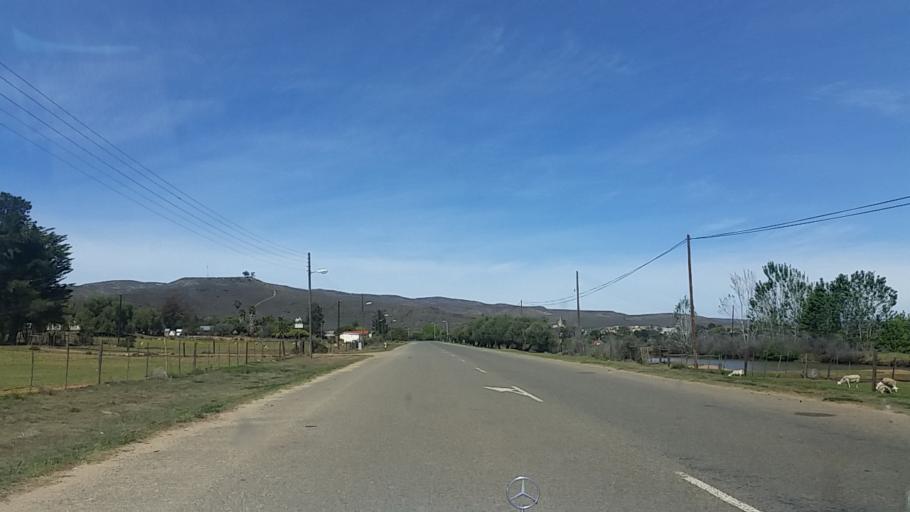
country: ZA
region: Western Cape
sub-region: Eden District Municipality
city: Knysna
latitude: -33.6468
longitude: 23.1362
